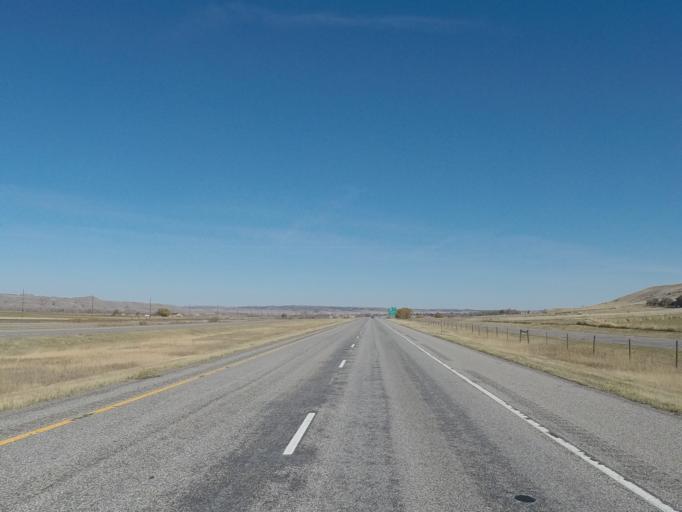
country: US
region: Montana
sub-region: Sweet Grass County
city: Big Timber
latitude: 45.8151
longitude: -109.9983
